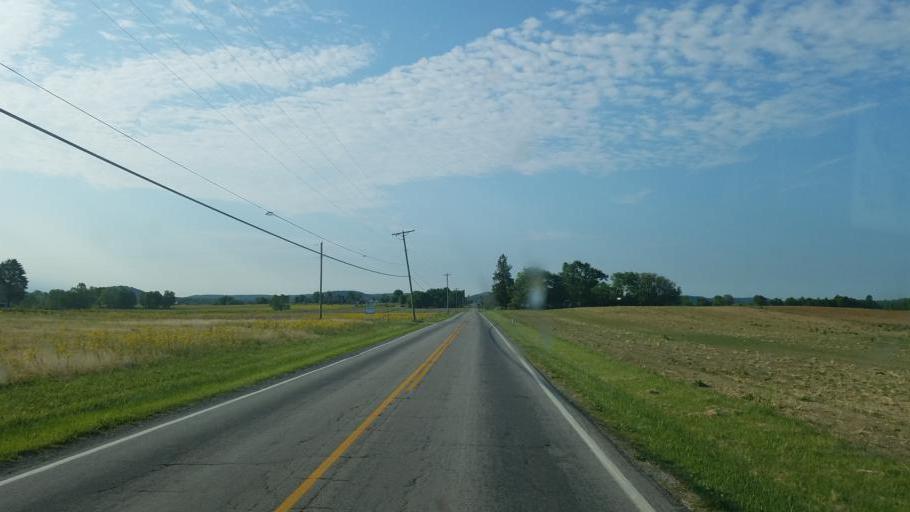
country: US
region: Ohio
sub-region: Highland County
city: Greenfield
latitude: 39.2283
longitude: -83.4257
